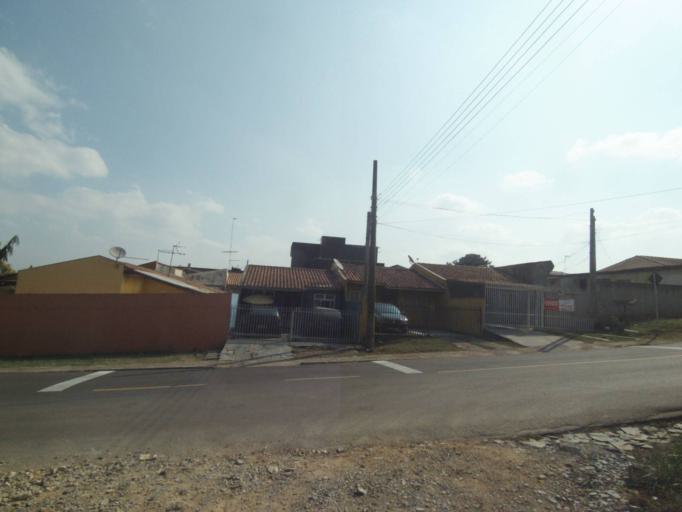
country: BR
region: Parana
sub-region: Sao Jose Dos Pinhais
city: Sao Jose dos Pinhais
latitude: -25.5172
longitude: -49.2472
